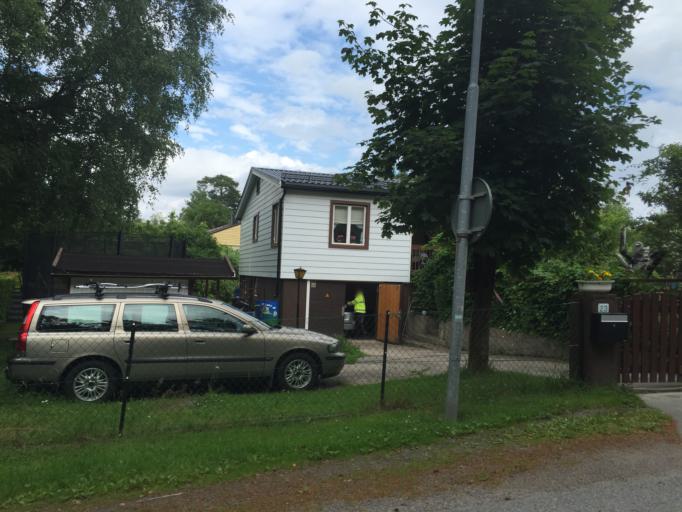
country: SE
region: Stockholm
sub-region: Botkyrka Kommun
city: Tullinge
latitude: 59.1951
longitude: 17.8922
